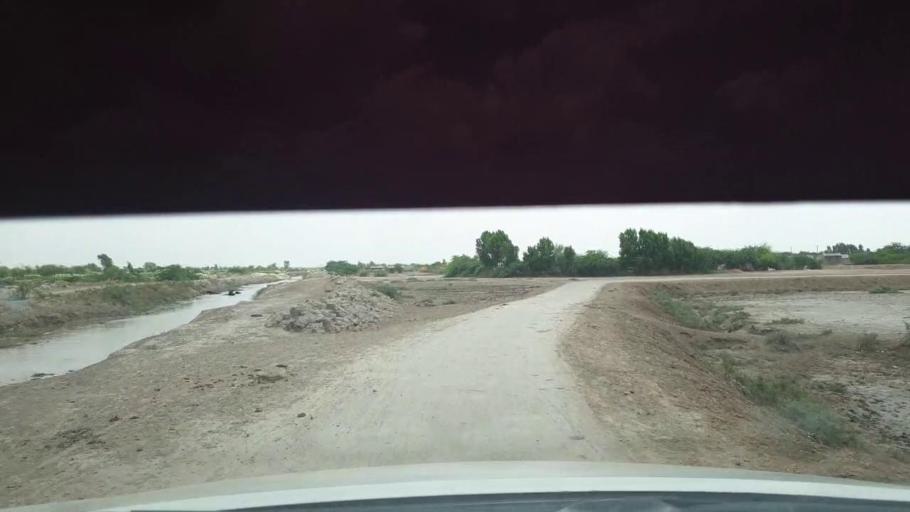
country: PK
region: Sindh
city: Kadhan
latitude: 24.5478
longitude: 69.1190
